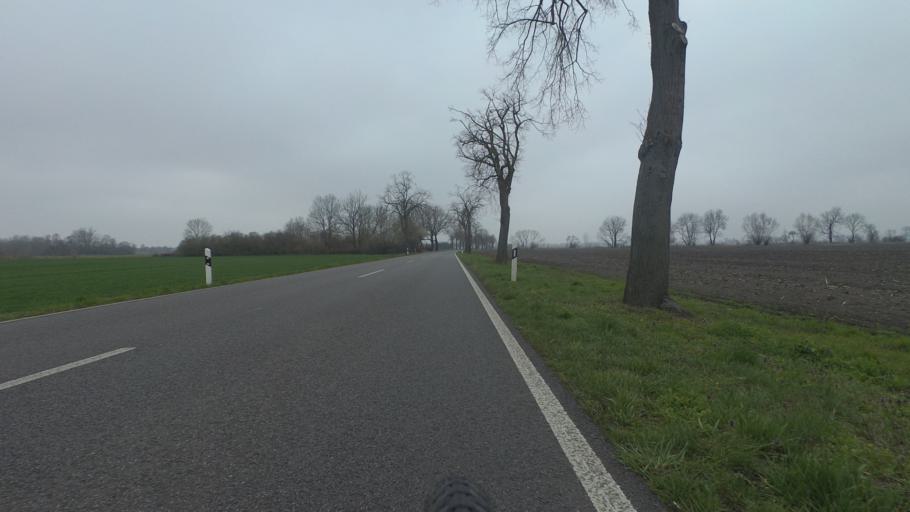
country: DE
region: Brandenburg
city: Nauen
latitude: 52.6205
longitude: 12.8700
